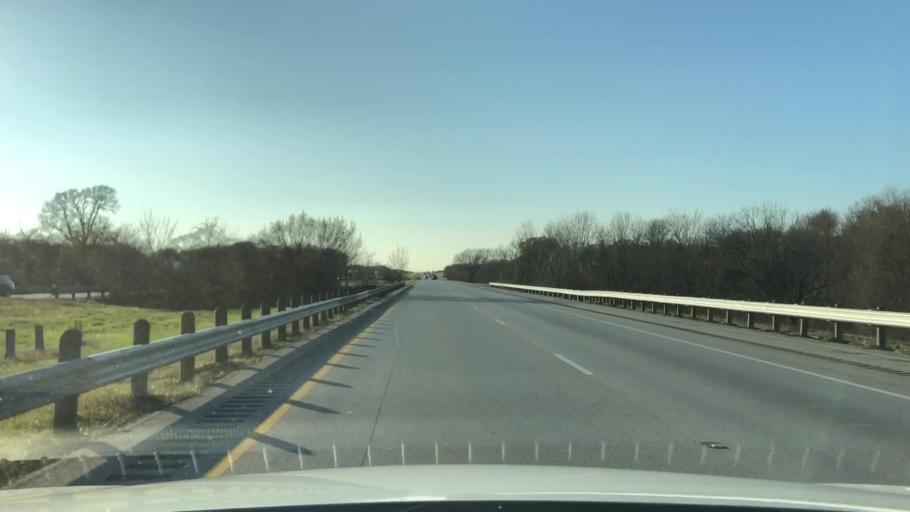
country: US
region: Texas
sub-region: Fayette County
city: Flatonia
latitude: 29.6922
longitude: -97.1843
